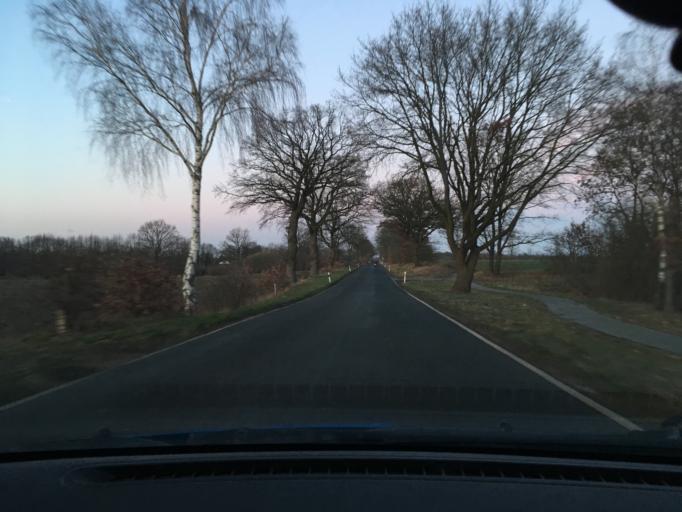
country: DE
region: Schleswig-Holstein
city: Fitzen
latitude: 53.4877
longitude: 10.6417
